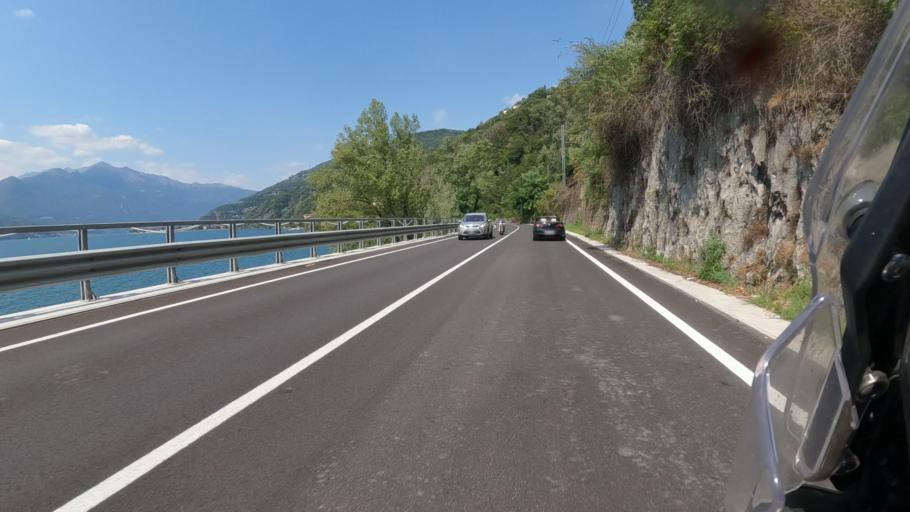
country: IT
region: Lombardy
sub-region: Provincia di Varese
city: Luino
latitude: 46.0159
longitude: 8.7516
